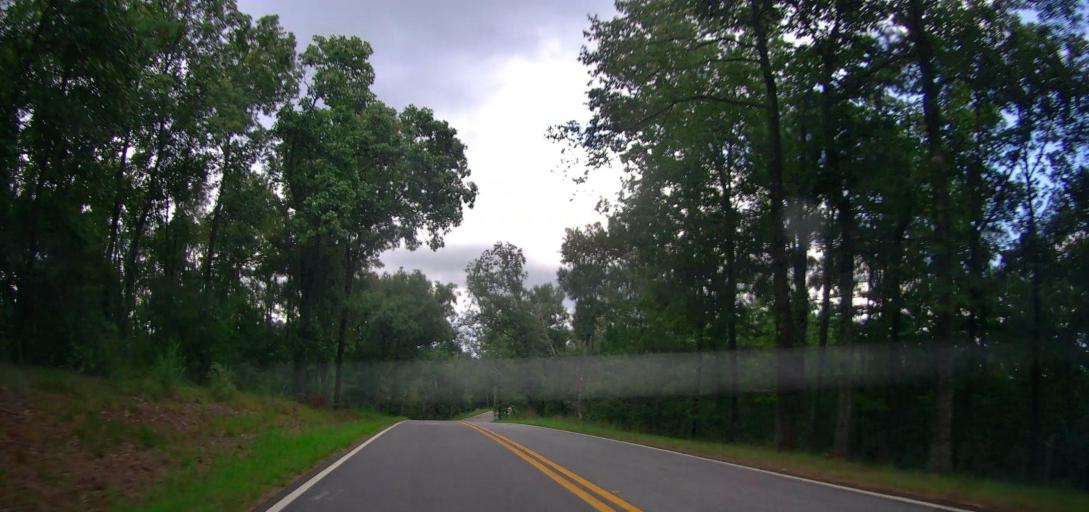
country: US
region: Georgia
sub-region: Harris County
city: Pine Mountain
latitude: 32.8447
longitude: -84.7989
